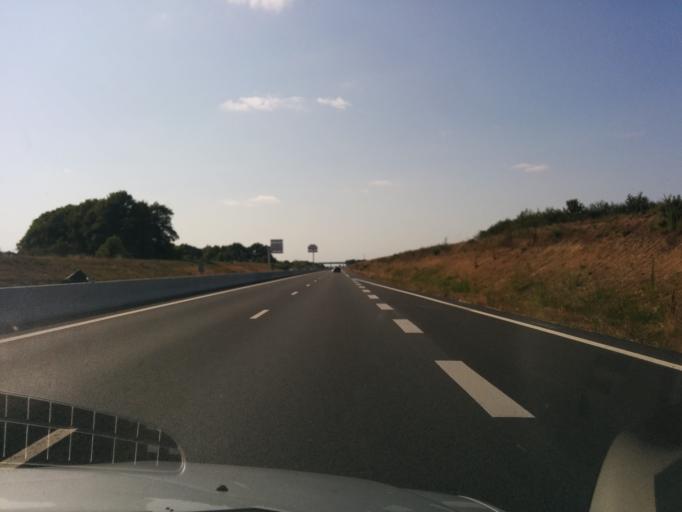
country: FR
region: Pays de la Loire
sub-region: Departement de Maine-et-Loire
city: La Tessoualle
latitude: 47.0253
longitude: -0.8860
